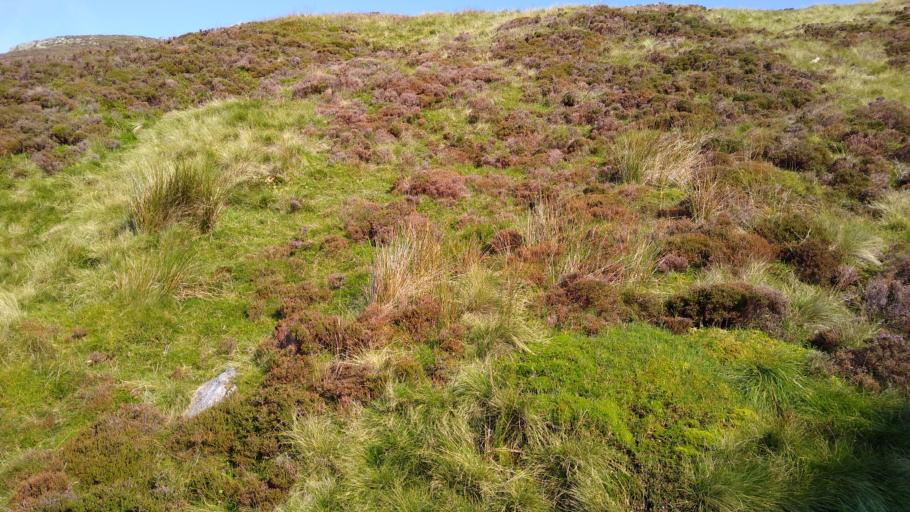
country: GB
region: England
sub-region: Cumbria
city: Cockermouth
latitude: 54.5332
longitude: -3.3625
